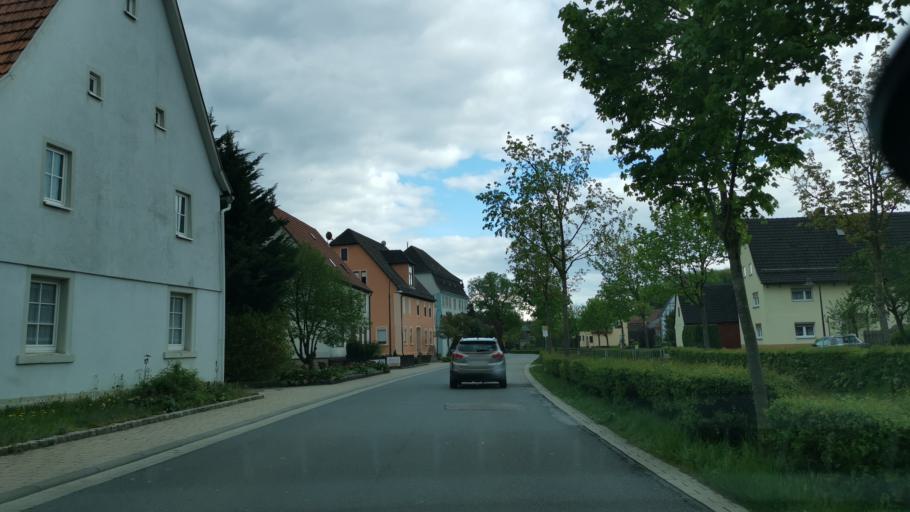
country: DE
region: Baden-Wuerttemberg
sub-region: Karlsruhe Region
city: Osterburken
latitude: 49.4732
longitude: 9.4105
